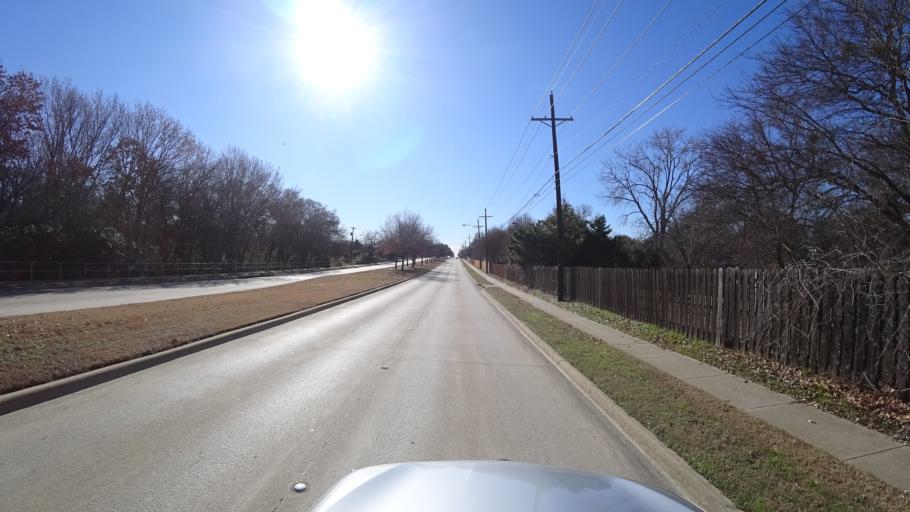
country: US
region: Texas
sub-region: Denton County
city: Lewisville
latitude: 33.0162
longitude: -97.0193
